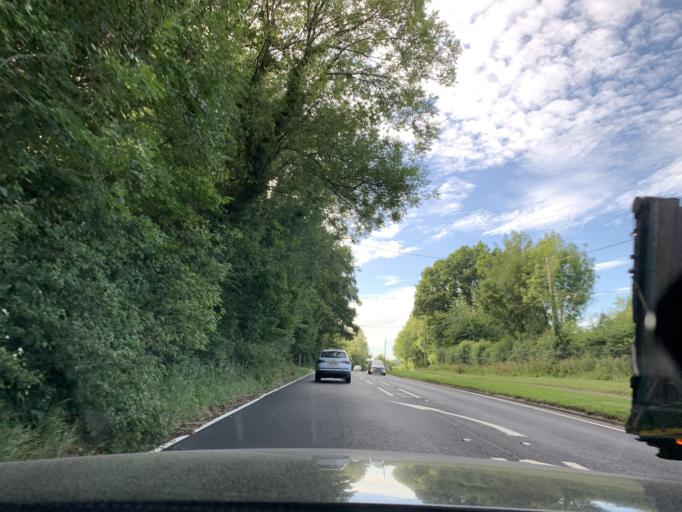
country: GB
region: England
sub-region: East Sussex
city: Robertsbridge
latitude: 51.0434
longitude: 0.4473
